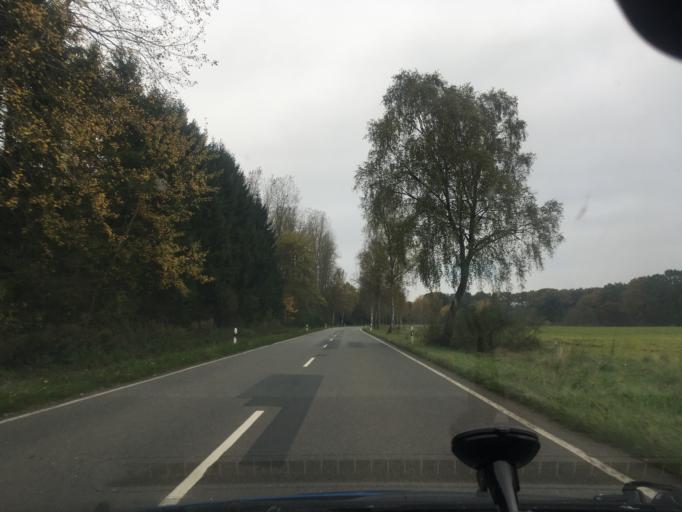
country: DE
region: Lower Saxony
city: Bispingen
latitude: 53.0240
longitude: 9.9984
